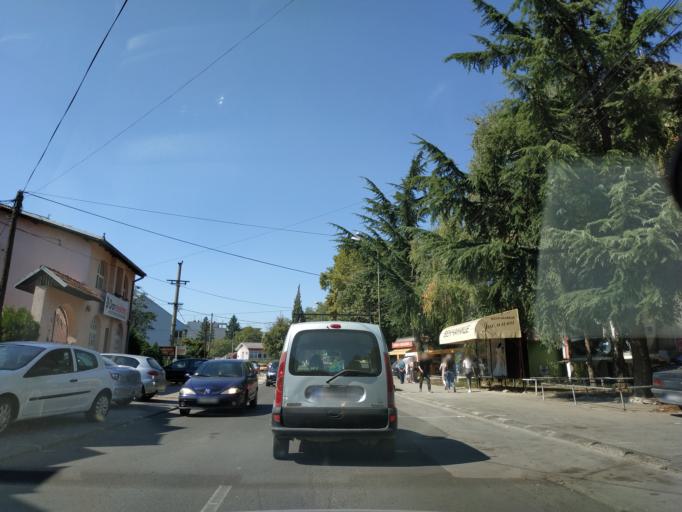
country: RS
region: Central Serbia
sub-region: Sumadijski Okrug
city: Arangelovac
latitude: 44.3045
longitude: 20.5631
